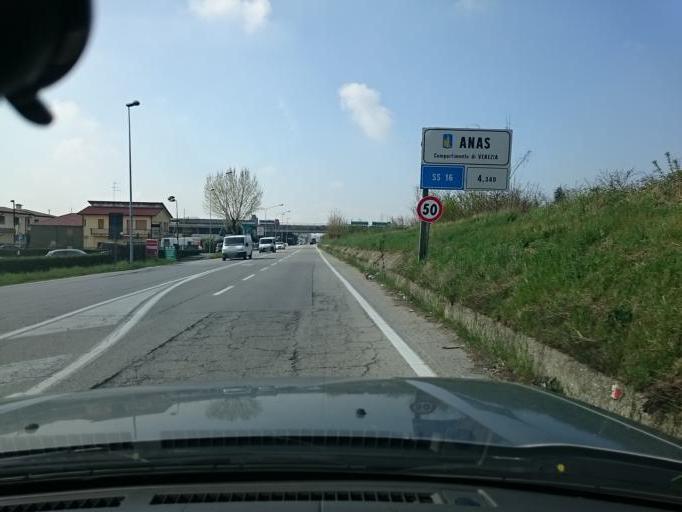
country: IT
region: Veneto
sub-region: Provincia di Padova
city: Mandriola-Sant'Agostino
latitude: 45.3764
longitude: 11.8505
